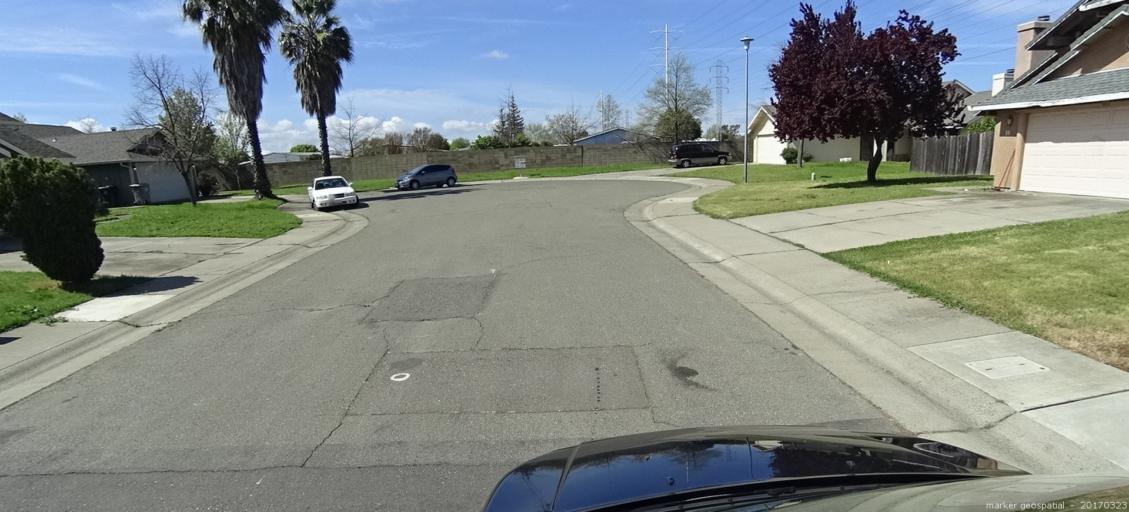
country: US
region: California
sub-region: Sacramento County
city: Florin
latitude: 38.5082
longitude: -121.4266
